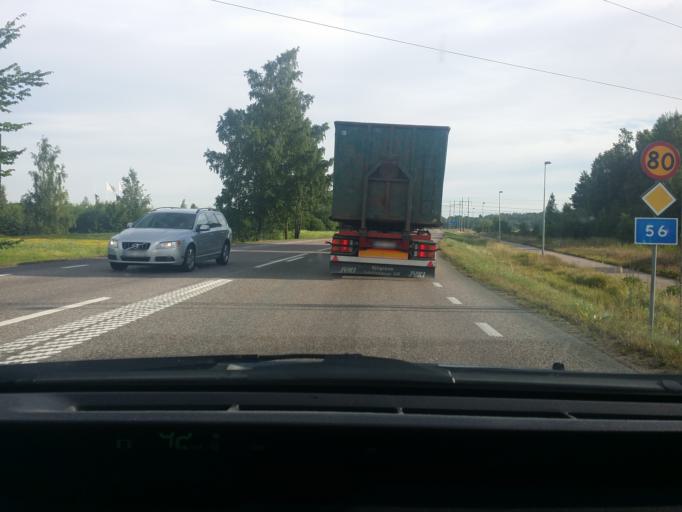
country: SE
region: Vaestmanland
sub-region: Vasteras
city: Hokasen
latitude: 59.6458
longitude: 16.5724
